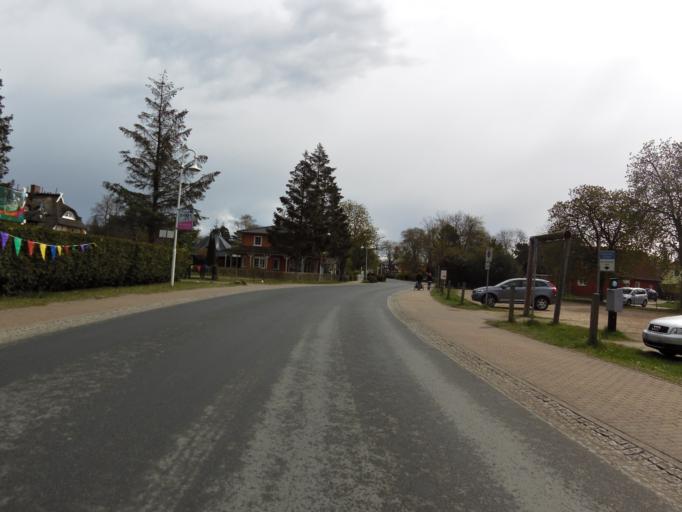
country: DE
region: Mecklenburg-Vorpommern
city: Ostseebad Prerow
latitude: 54.4474
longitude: 12.5639
